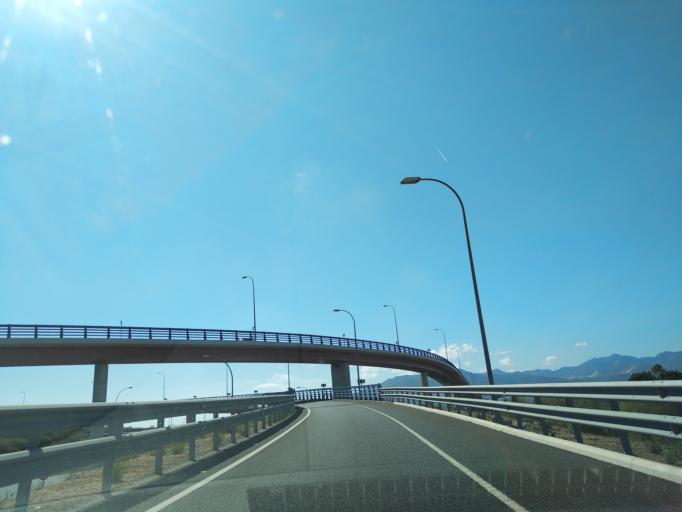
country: ES
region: Andalusia
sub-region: Provincia de Malaga
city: Alhaurin de la Torre
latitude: 36.7145
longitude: -4.5092
